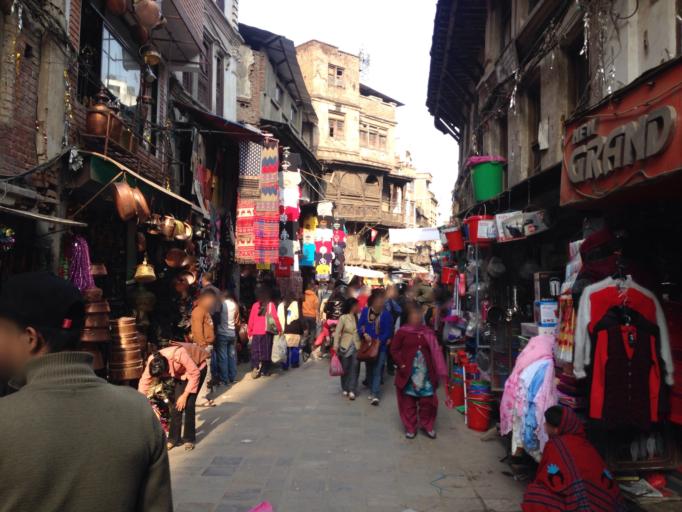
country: NP
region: Central Region
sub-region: Bagmati Zone
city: Kathmandu
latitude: 27.7073
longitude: 85.3118
